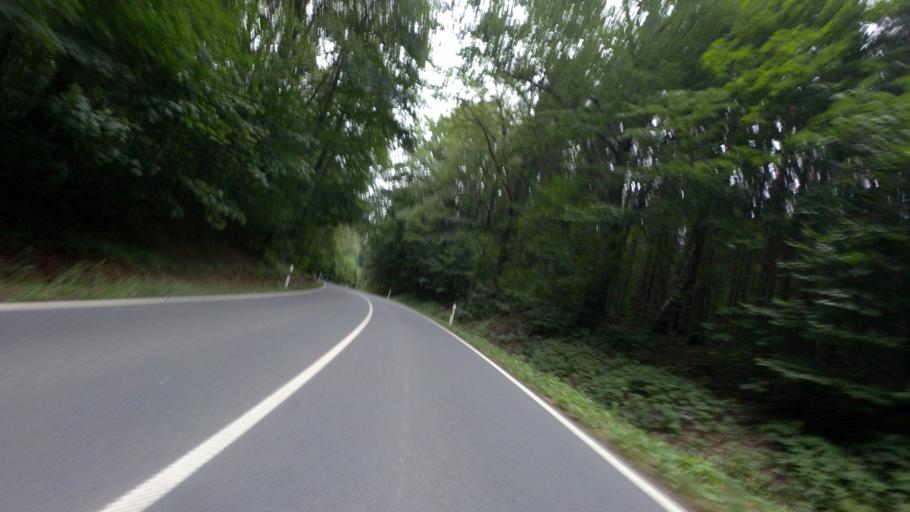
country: DE
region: Saxony
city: Berthelsdorf
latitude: 51.0870
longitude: 14.2040
